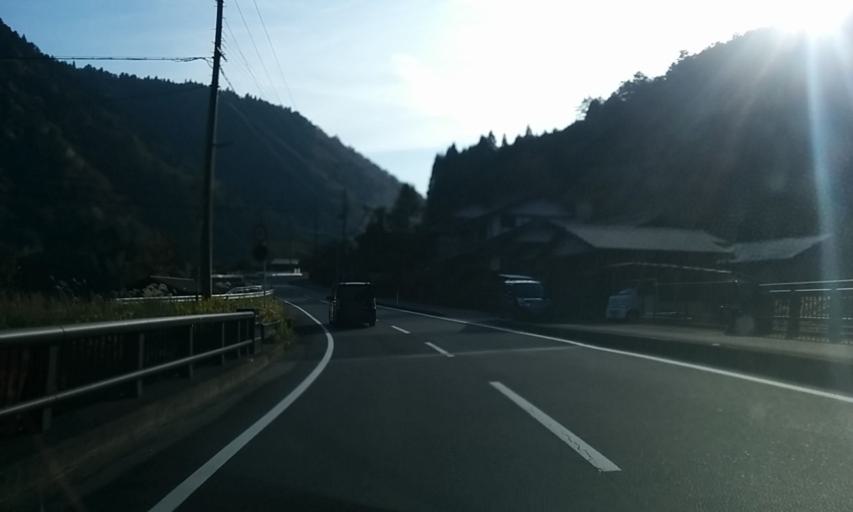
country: JP
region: Fukui
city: Obama
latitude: 35.2901
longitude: 135.5999
